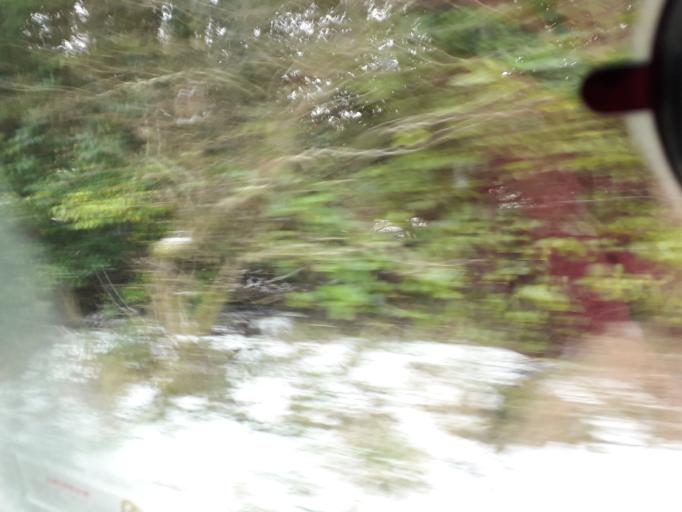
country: IE
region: Leinster
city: Ballyboden
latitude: 53.2397
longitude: -6.3160
